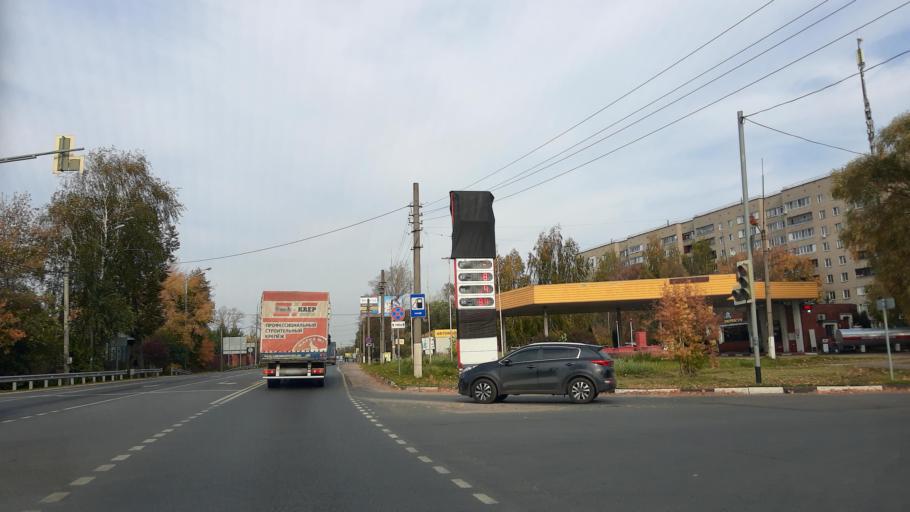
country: RU
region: Moskovskaya
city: Elektrostal'
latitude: 55.7621
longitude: 38.4361
